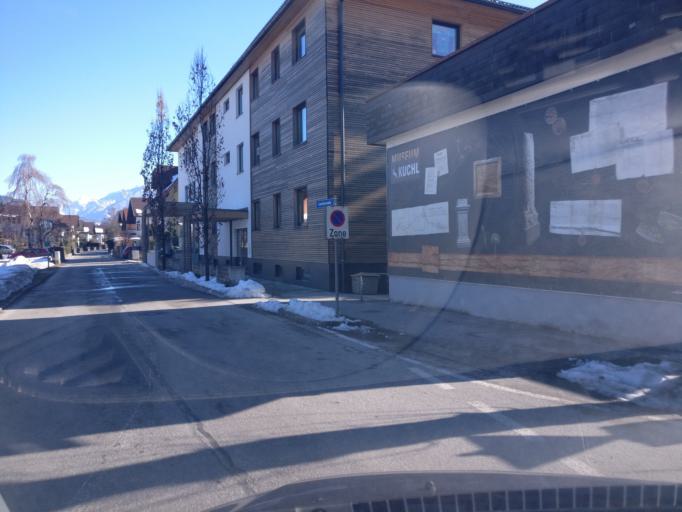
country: AT
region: Salzburg
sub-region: Politischer Bezirk Hallein
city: Kuchl
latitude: 47.6248
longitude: 13.1442
